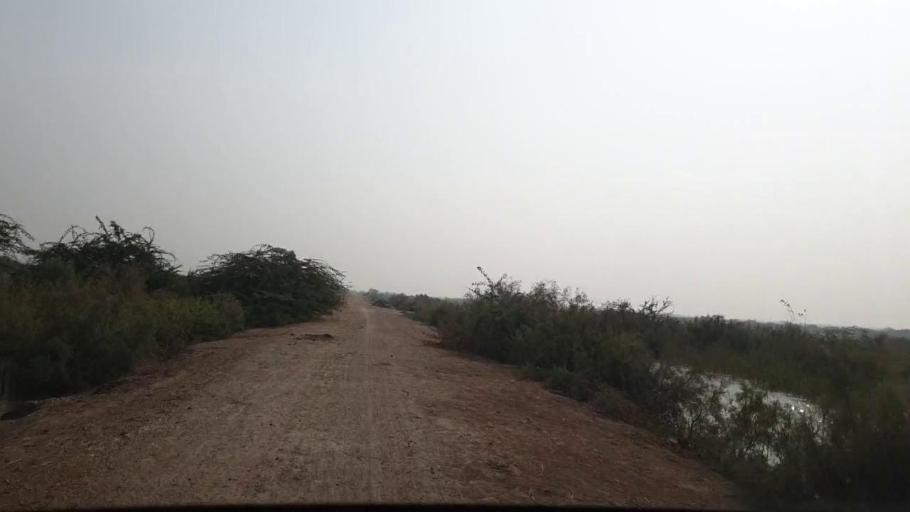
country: PK
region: Sindh
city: Jati
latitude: 24.2709
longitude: 68.4233
